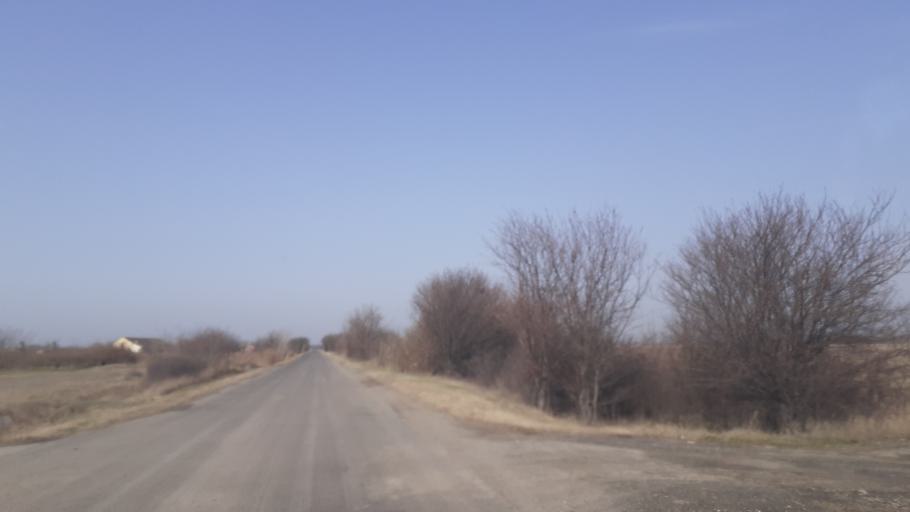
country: HU
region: Pest
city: Bugyi
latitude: 47.1268
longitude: 19.2084
